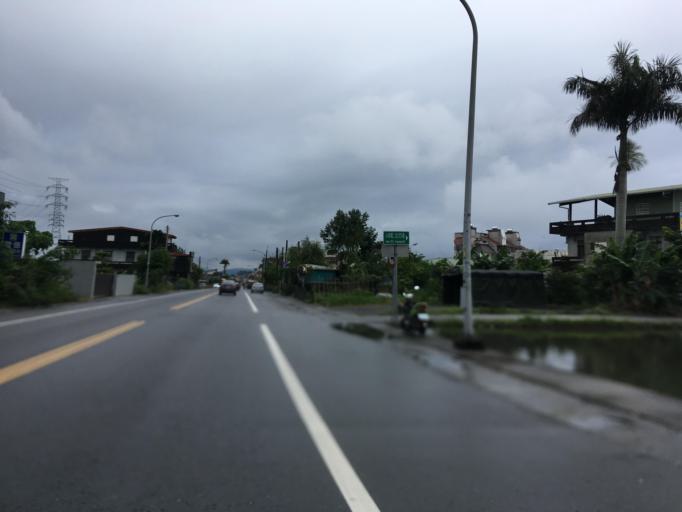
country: TW
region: Taiwan
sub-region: Yilan
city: Yilan
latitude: 24.6589
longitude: 121.7568
